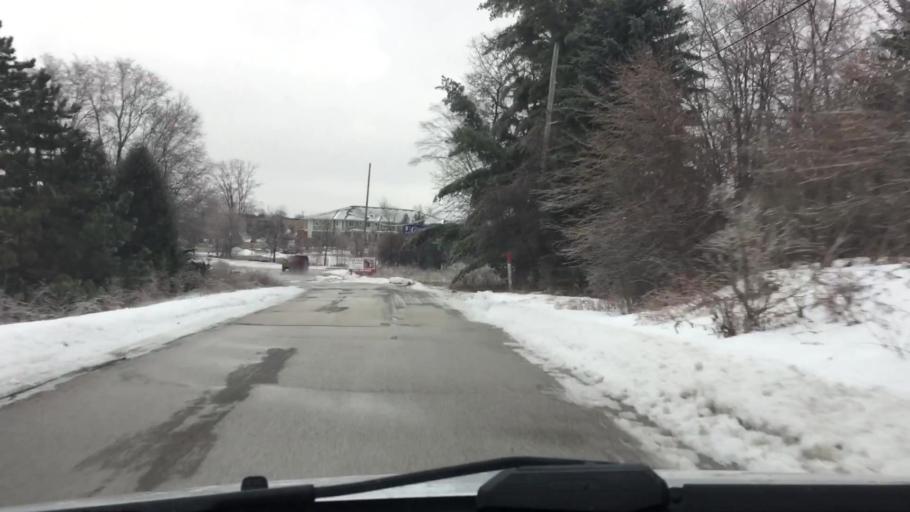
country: US
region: Wisconsin
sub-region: Waukesha County
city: Pewaukee
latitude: 43.0424
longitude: -88.2611
